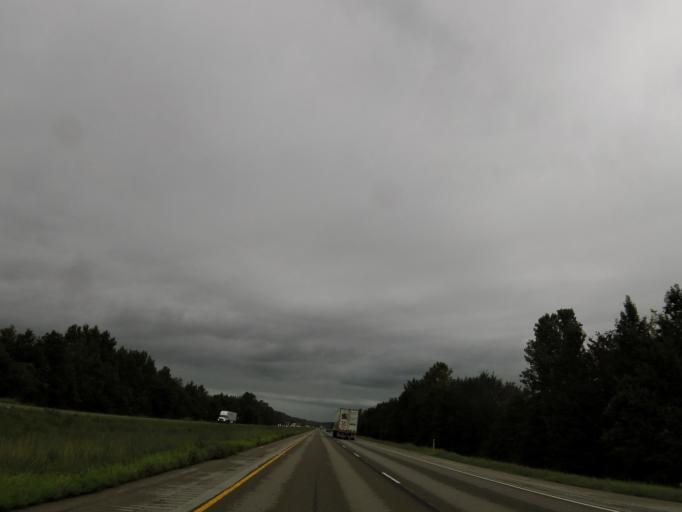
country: US
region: Illinois
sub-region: Massac County
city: Metropolis
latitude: 37.2902
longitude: -88.7494
